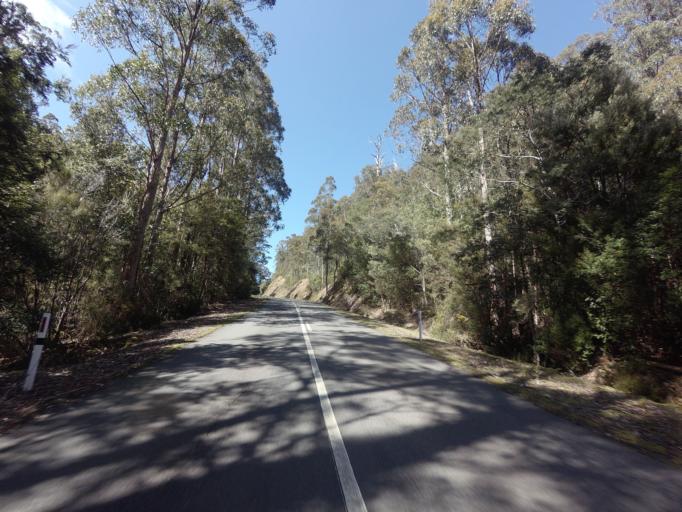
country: AU
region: Tasmania
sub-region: Derwent Valley
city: New Norfolk
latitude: -42.7427
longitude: 146.4988
